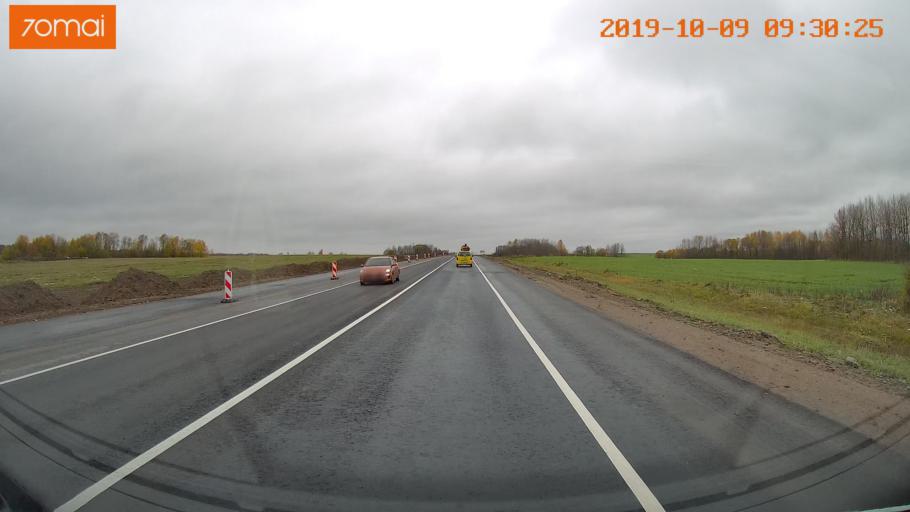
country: RU
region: Vologda
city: Vologda
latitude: 59.1398
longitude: 39.9492
